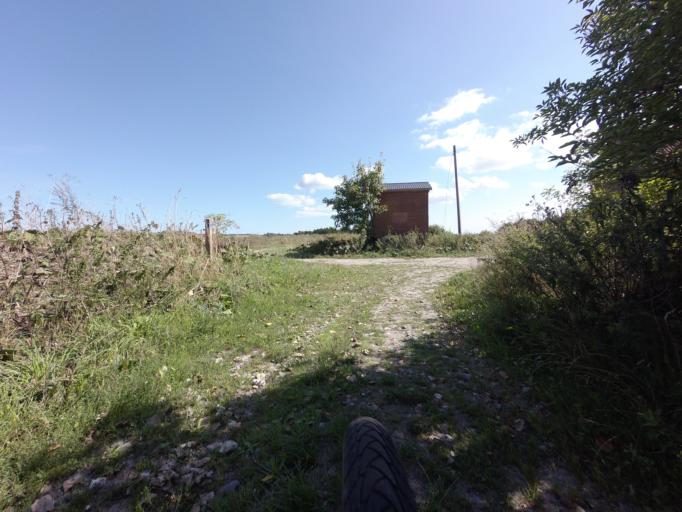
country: DK
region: Zealand
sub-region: Vordingborg Kommune
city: Stege
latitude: 55.0205
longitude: 12.4309
